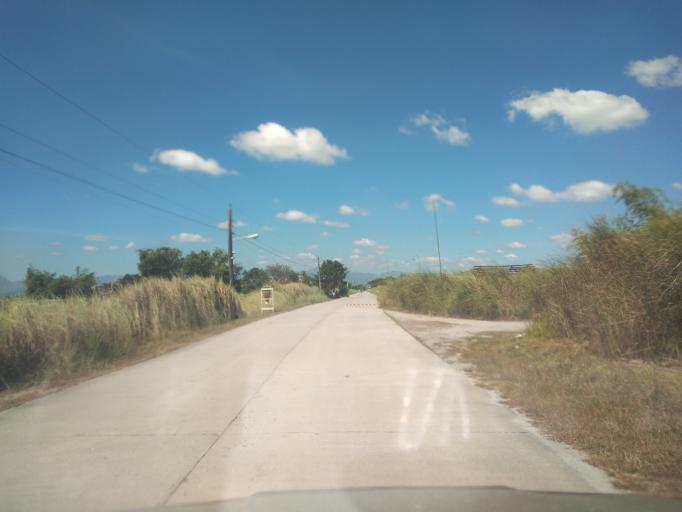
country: PH
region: Central Luzon
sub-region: Province of Pampanga
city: Balas
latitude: 15.0534
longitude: 120.6062
